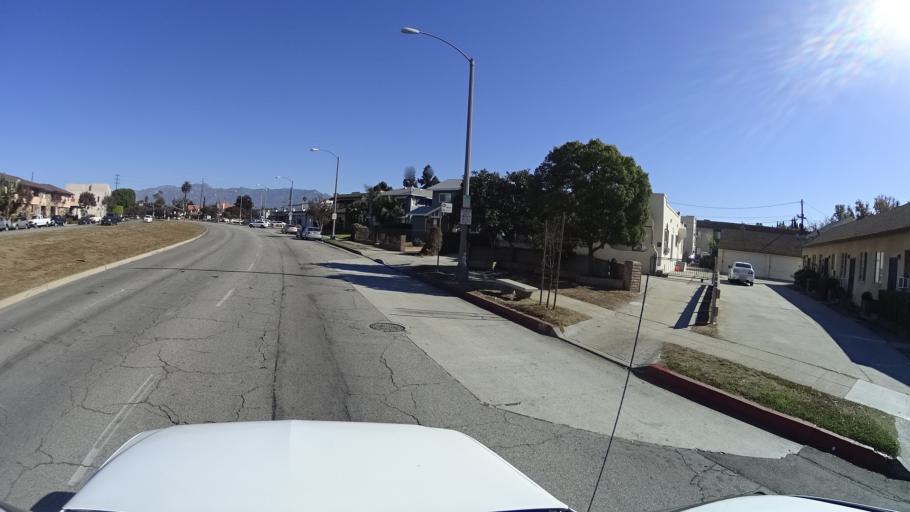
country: US
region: California
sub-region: Los Angeles County
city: South Pasadena
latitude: 34.0967
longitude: -118.1559
